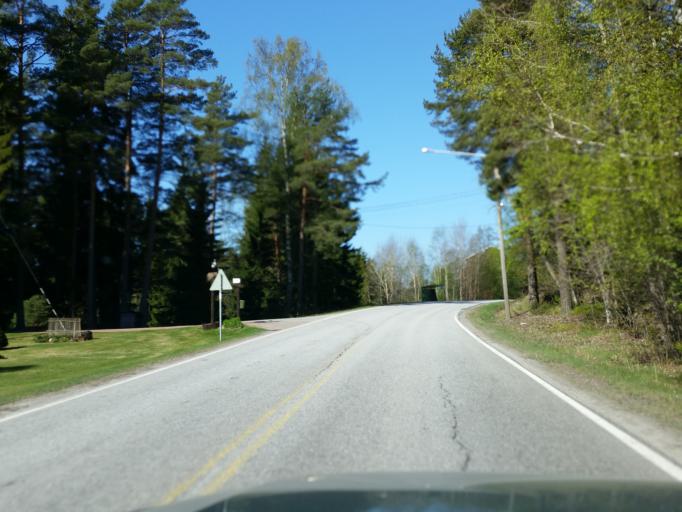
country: FI
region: Uusimaa
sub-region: Helsinki
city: Lohja
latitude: 60.1738
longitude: 24.1218
